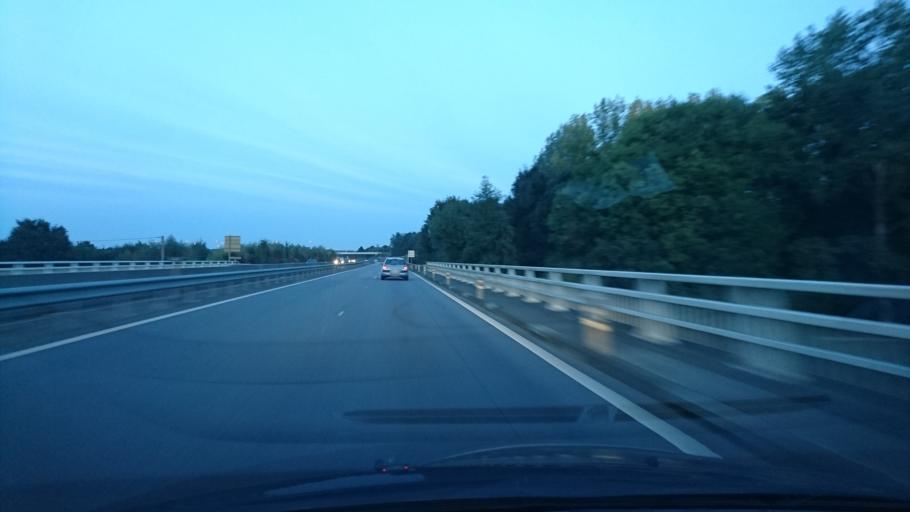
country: FR
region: Brittany
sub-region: Departement d'Ille-et-Vilaine
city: Bruz
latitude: 48.0257
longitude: -1.7737
